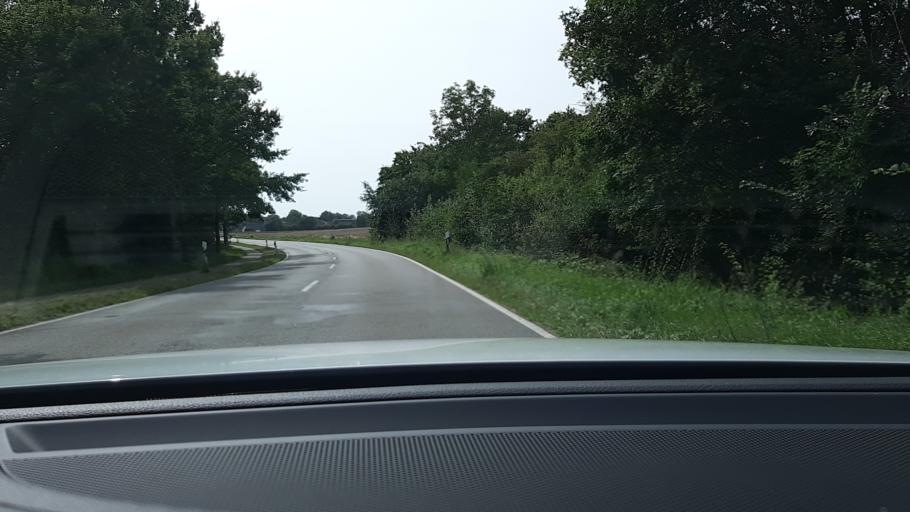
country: DE
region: Schleswig-Holstein
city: Heilshoop
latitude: 53.8792
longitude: 10.5230
